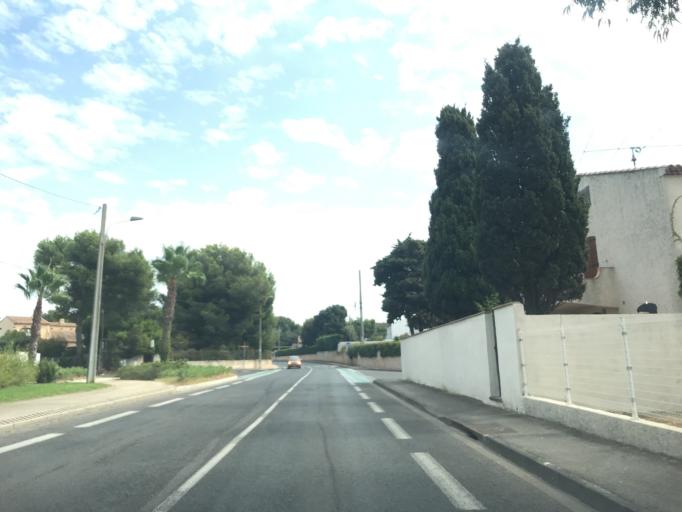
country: FR
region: Provence-Alpes-Cote d'Azur
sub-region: Departement du Var
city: Sanary-sur-Mer
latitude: 43.0870
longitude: 5.8153
